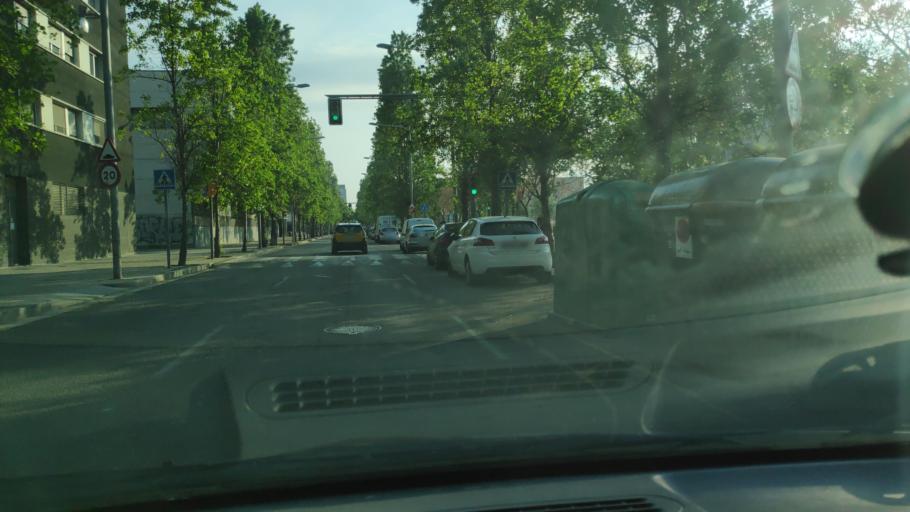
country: ES
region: Catalonia
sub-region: Provincia de Barcelona
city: Sant Adria de Besos
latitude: 41.4162
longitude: 2.2223
